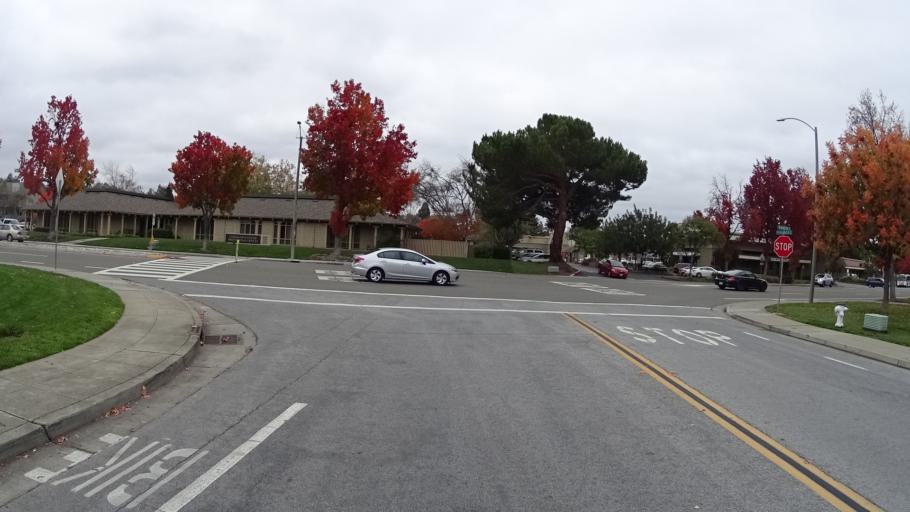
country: US
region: California
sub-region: Santa Clara County
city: Sunnyvale
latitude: 37.3599
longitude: -122.0253
